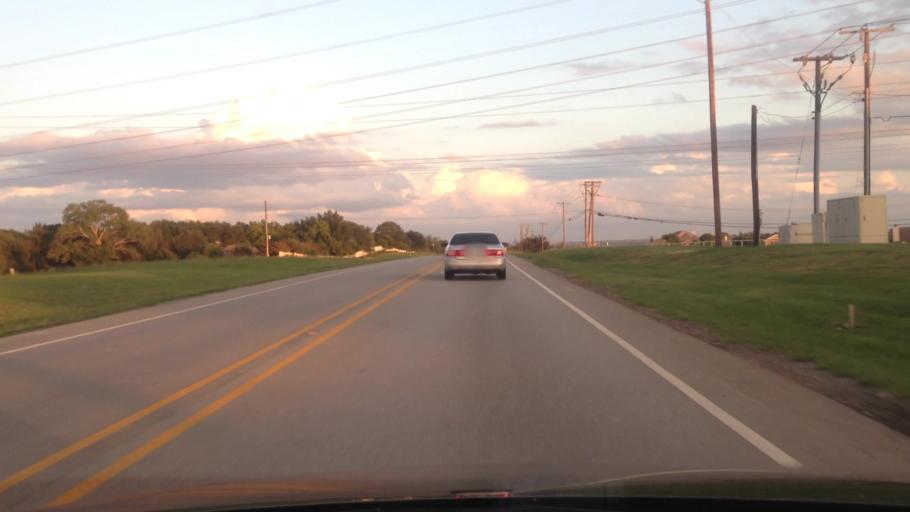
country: US
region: Texas
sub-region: Tarrant County
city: Benbrook
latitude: 32.6717
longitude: -97.4944
